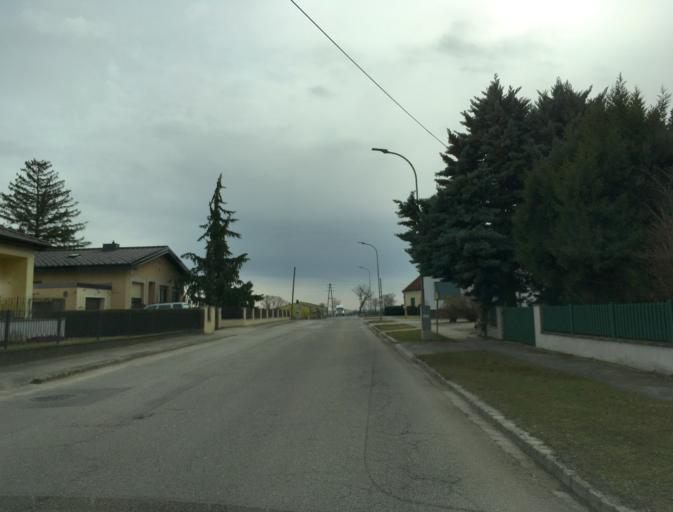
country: AT
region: Lower Austria
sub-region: Politischer Bezirk Ganserndorf
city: Markgrafneusiedl
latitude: 48.2622
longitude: 16.6363
